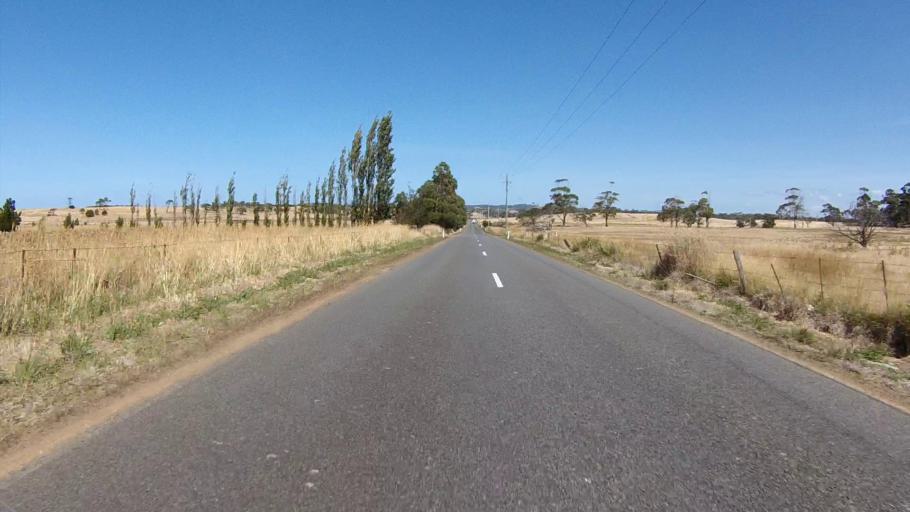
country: AU
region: Tasmania
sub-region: Sorell
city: Sorell
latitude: -42.2703
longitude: 148.0038
